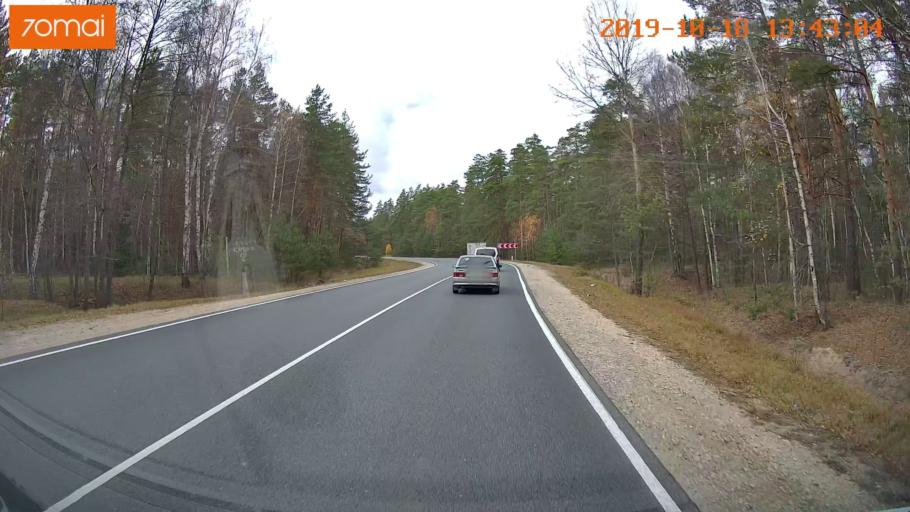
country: RU
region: Rjazan
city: Solotcha
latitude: 54.9279
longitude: 39.9789
